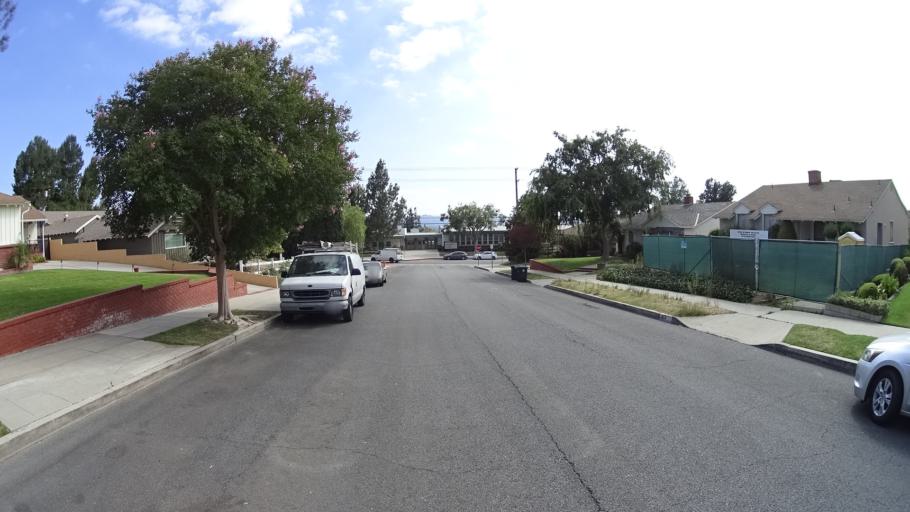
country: US
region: California
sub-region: Los Angeles County
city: Burbank
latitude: 34.1954
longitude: -118.3106
